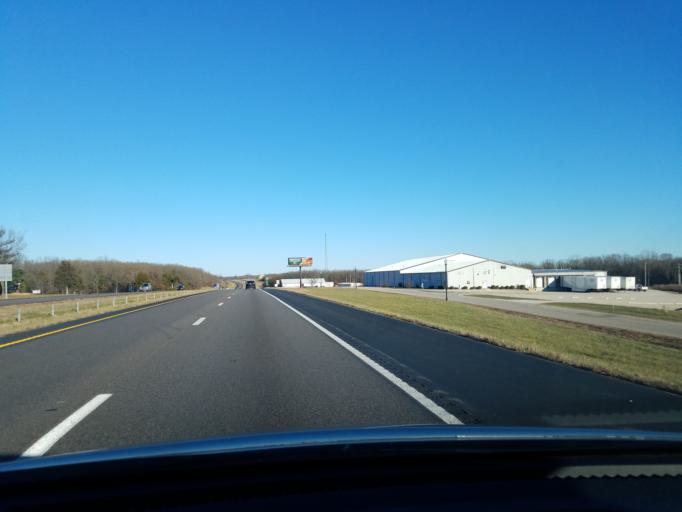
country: US
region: Missouri
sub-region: Phelps County
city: Saint James
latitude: 38.0119
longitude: -91.5969
